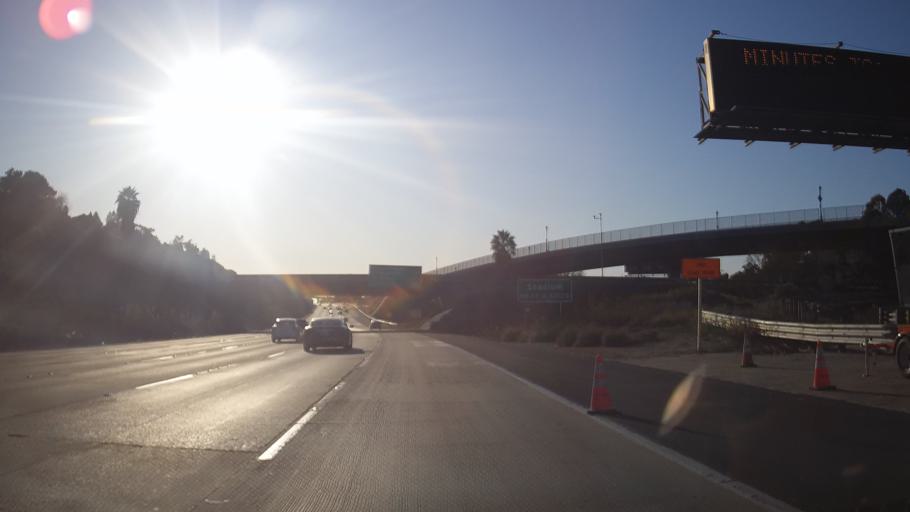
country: US
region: California
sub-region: San Diego County
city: La Mesa
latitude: 32.7823
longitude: -117.0862
